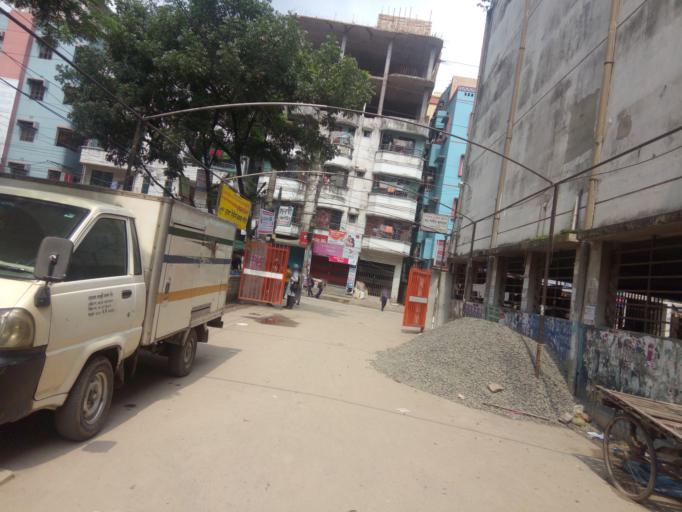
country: BD
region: Dhaka
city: Paltan
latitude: 23.7527
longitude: 90.4407
